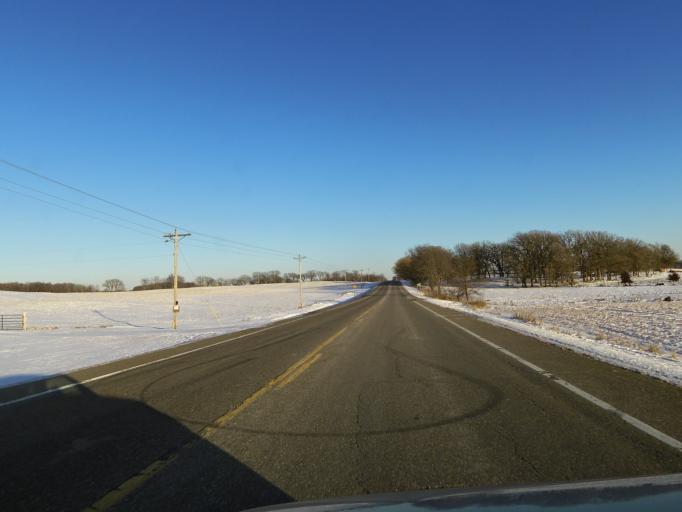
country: US
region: Minnesota
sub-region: Scott County
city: Elko New Market
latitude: 44.5438
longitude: -93.2706
